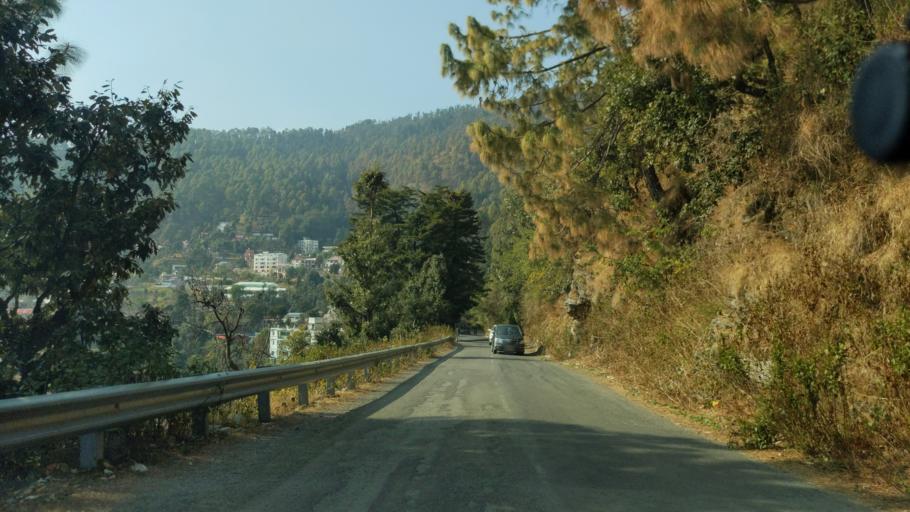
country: IN
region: Uttarakhand
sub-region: Naini Tal
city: Bhowali
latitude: 29.3909
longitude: 79.5349
